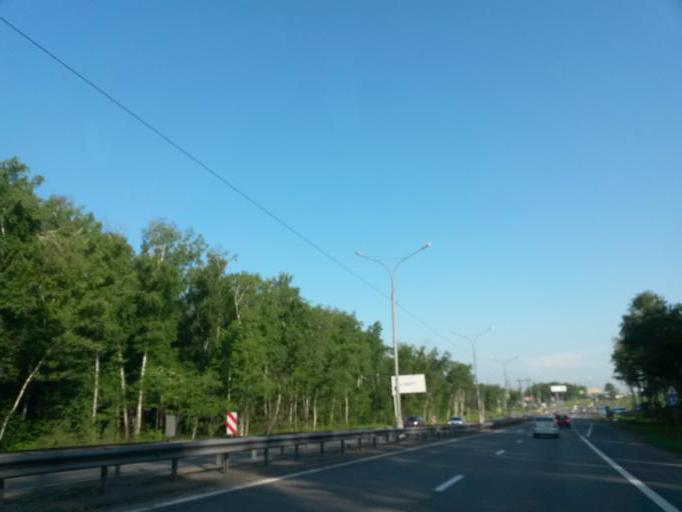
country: RU
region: Moskovskaya
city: Petrovskaya
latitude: 55.5550
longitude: 37.7820
